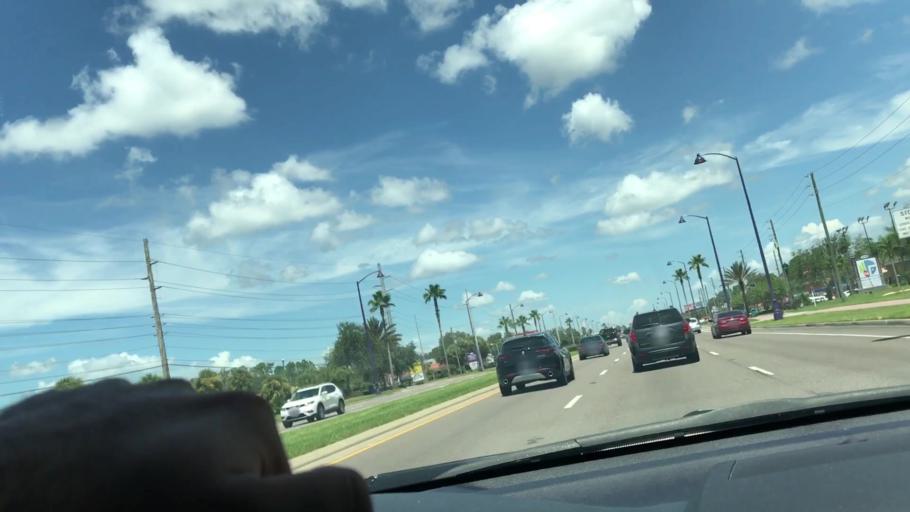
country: US
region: Florida
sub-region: Osceola County
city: Kissimmee
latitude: 28.3084
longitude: -81.4645
